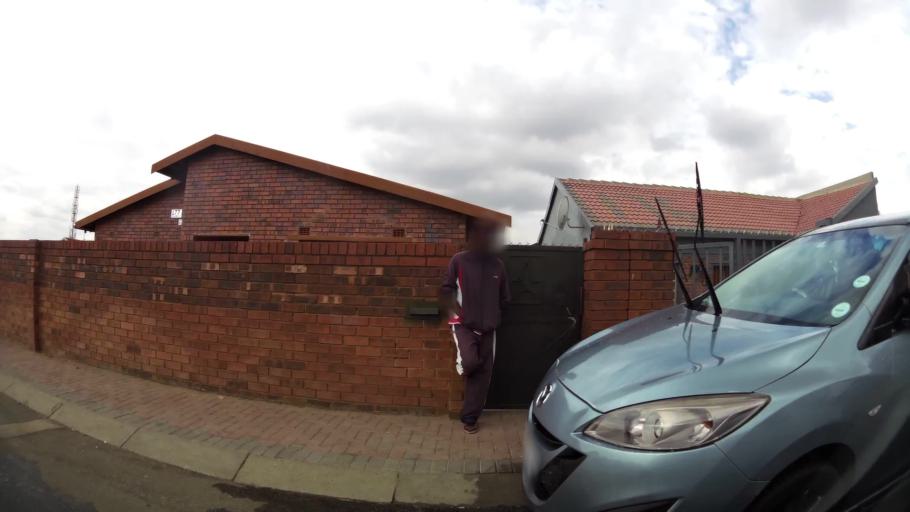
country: ZA
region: Gauteng
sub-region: City of Johannesburg Metropolitan Municipality
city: Soweto
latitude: -26.2712
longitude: 27.8729
